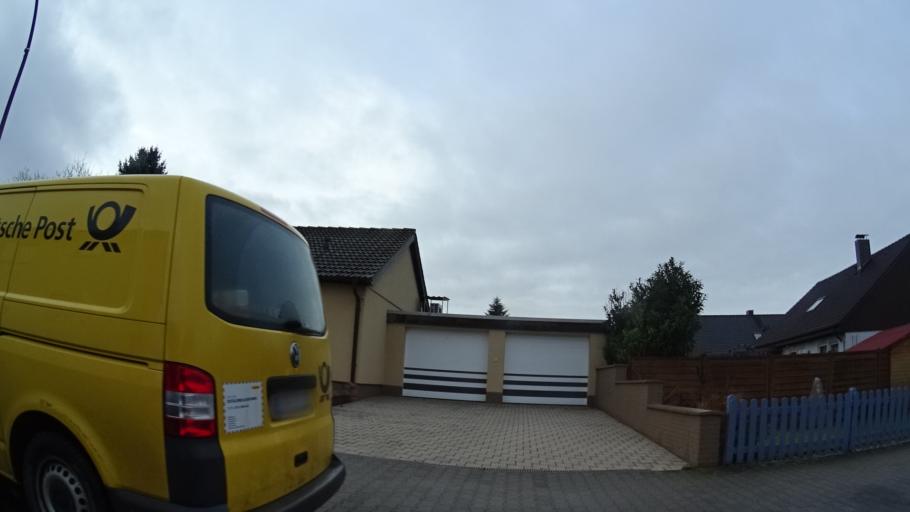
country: DE
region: Baden-Wuerttemberg
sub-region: Karlsruhe Region
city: Philippsburg
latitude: 49.2311
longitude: 8.4136
